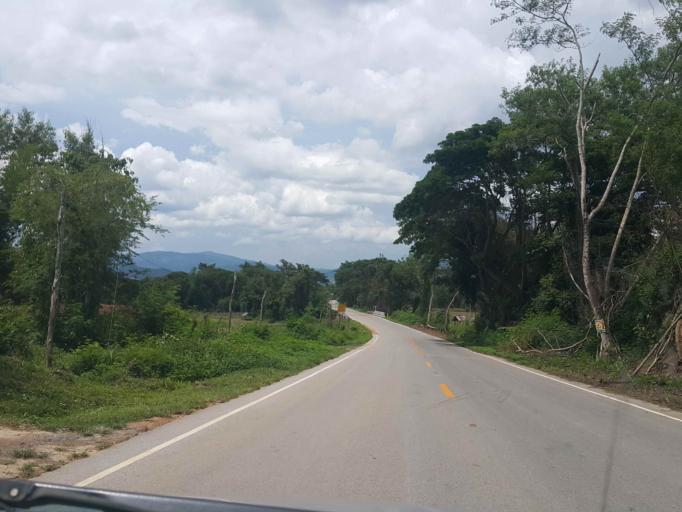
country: TH
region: Nan
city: Ban Luang
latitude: 18.8444
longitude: 100.4200
